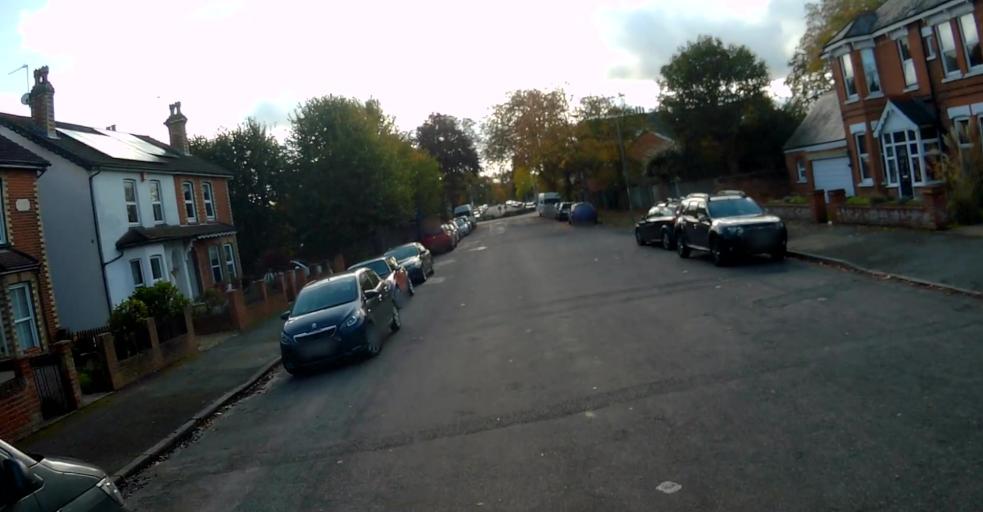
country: GB
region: England
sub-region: Hampshire
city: Farnborough
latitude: 51.2766
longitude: -0.7548
